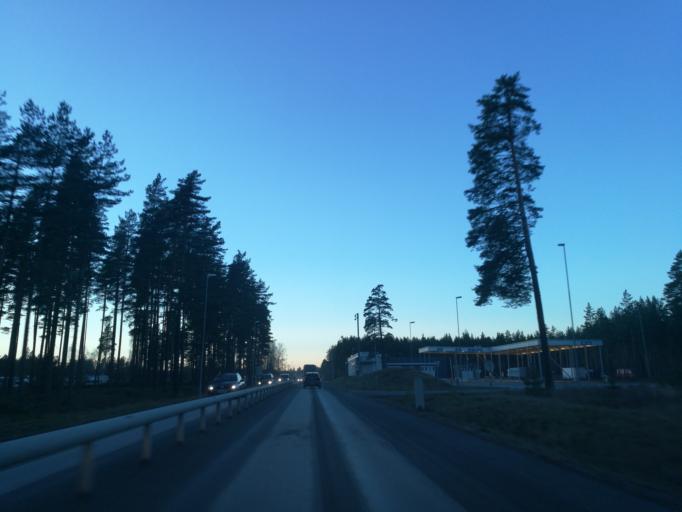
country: SE
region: Vaermland
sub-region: Eda Kommun
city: Charlottenberg
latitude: 59.9325
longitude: 12.2347
